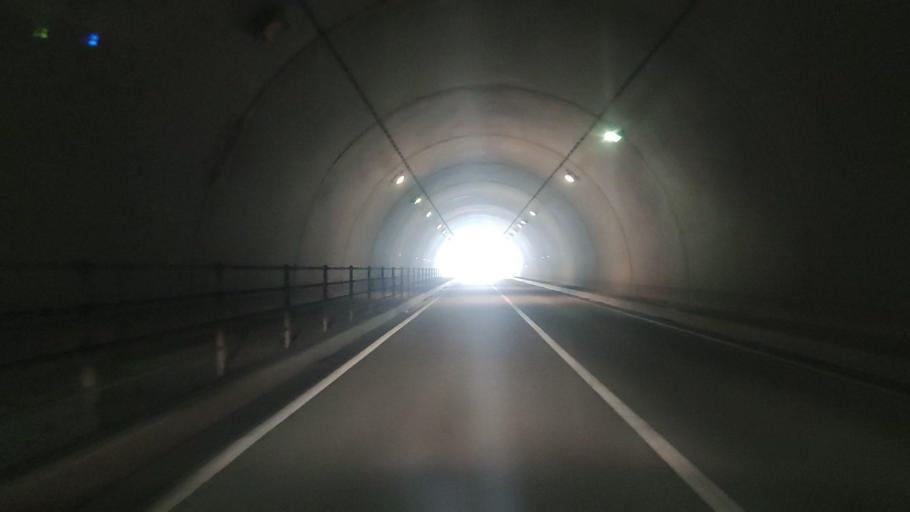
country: JP
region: Oita
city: Saiki
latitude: 32.8052
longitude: 131.8974
